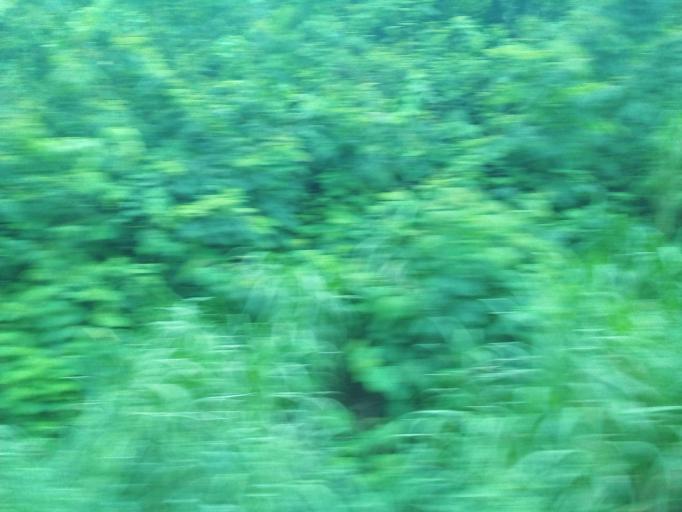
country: BR
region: Minas Gerais
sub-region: Joao Monlevade
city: Joao Monlevade
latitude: -19.8260
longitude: -43.1150
